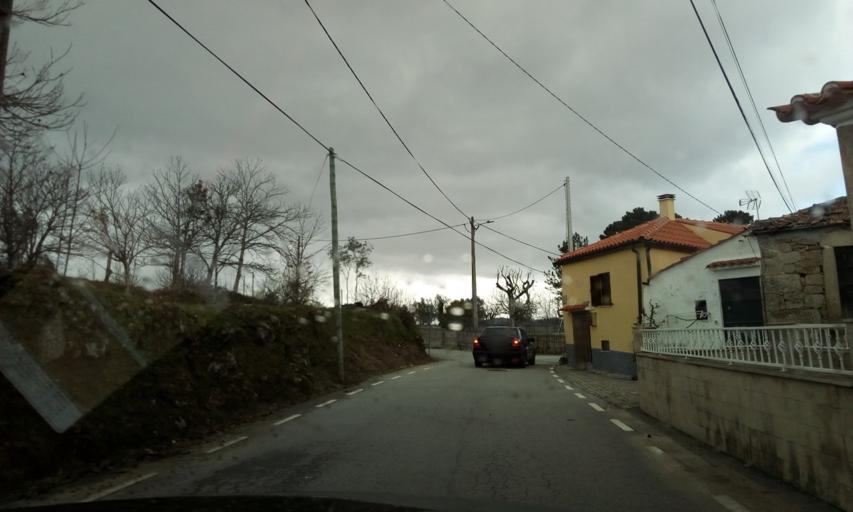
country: PT
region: Guarda
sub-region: Fornos de Algodres
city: Fornos de Algodres
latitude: 40.6379
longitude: -7.5839
